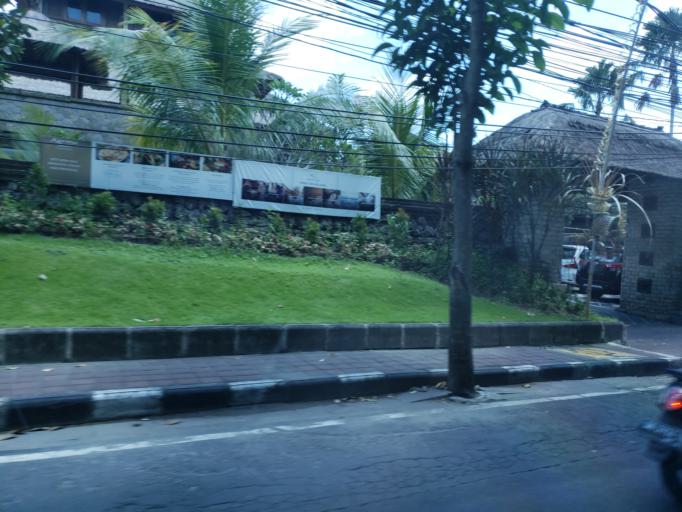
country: ID
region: Bali
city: Jimbaran
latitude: -8.7795
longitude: 115.1683
